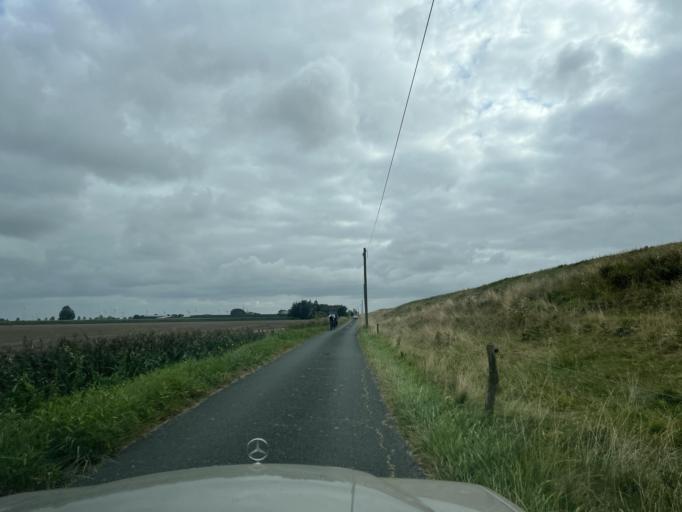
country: DE
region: Schleswig-Holstein
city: Groven
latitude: 54.3181
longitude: 8.9849
